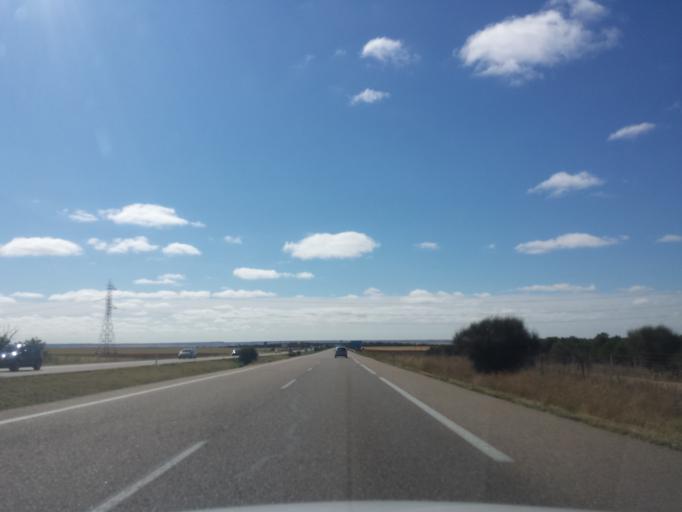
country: ES
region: Castille and Leon
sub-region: Provincia de Zamora
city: Quintanilla del Monte
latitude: 41.8077
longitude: -5.3538
